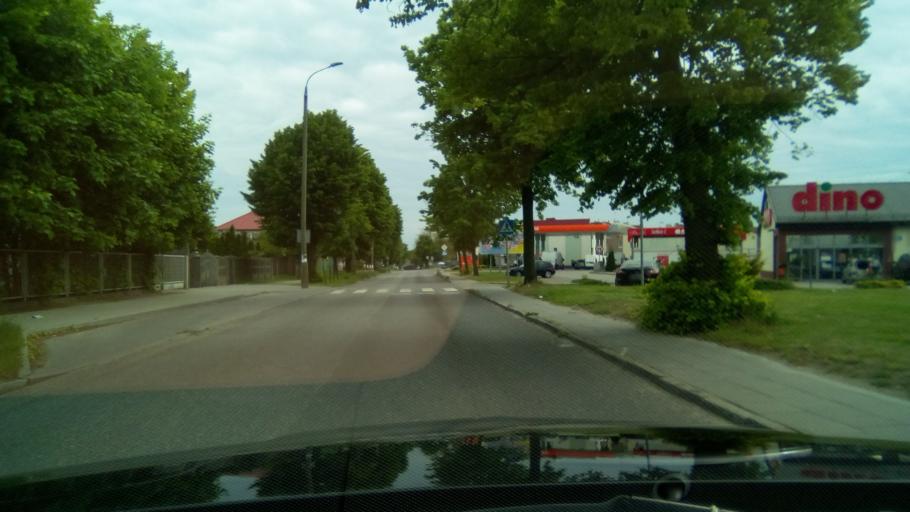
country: PL
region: Greater Poland Voivodeship
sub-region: Powiat gnieznienski
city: Gniezno
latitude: 52.5177
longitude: 17.6003
